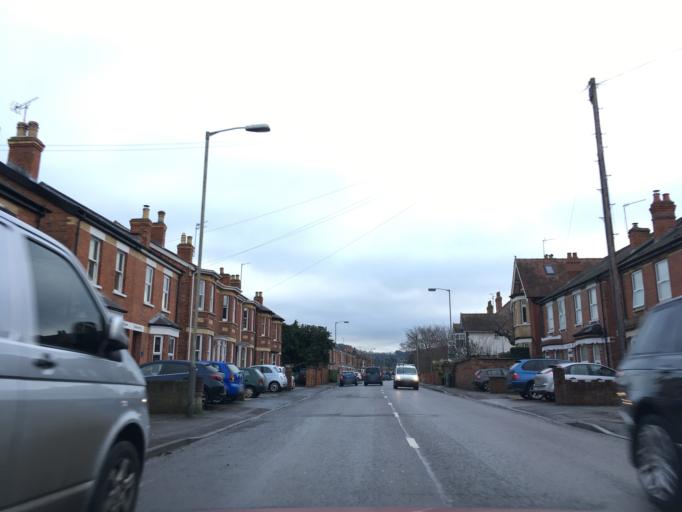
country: GB
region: England
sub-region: Gloucestershire
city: Charlton Kings
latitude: 51.8830
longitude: -2.0559
